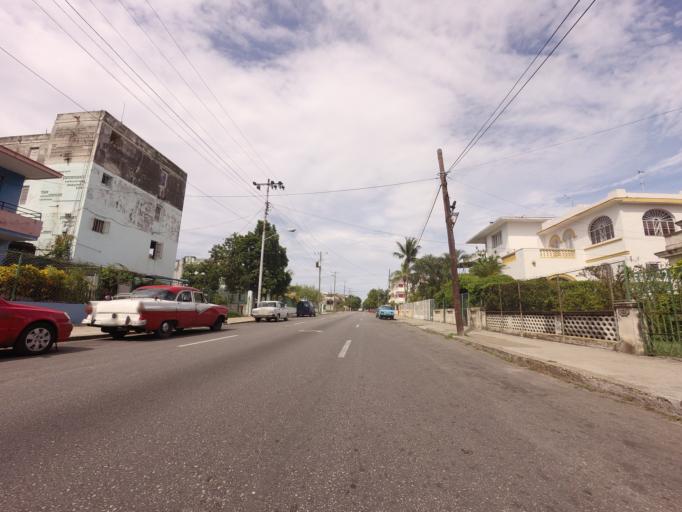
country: CU
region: La Habana
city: Havana
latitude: 23.1261
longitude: -82.4069
